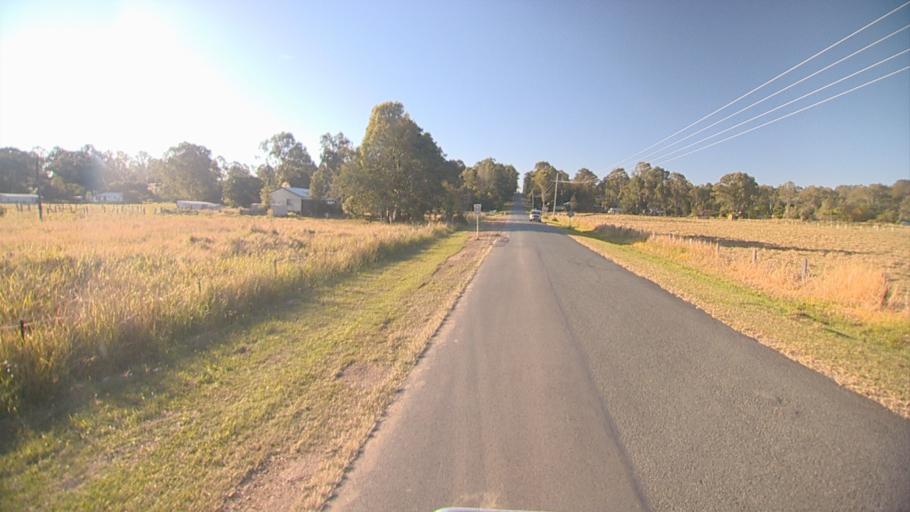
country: AU
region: Queensland
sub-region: Logan
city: Chambers Flat
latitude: -27.7830
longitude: 153.1350
